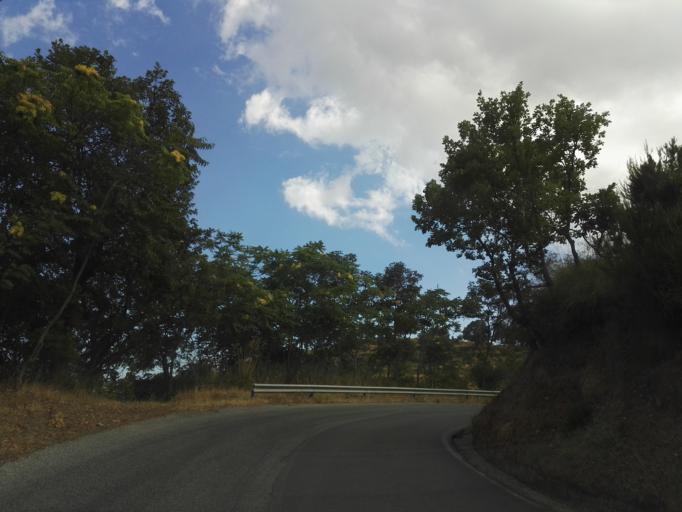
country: IT
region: Calabria
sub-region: Provincia di Reggio Calabria
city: Riace
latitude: 38.4244
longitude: 16.4840
